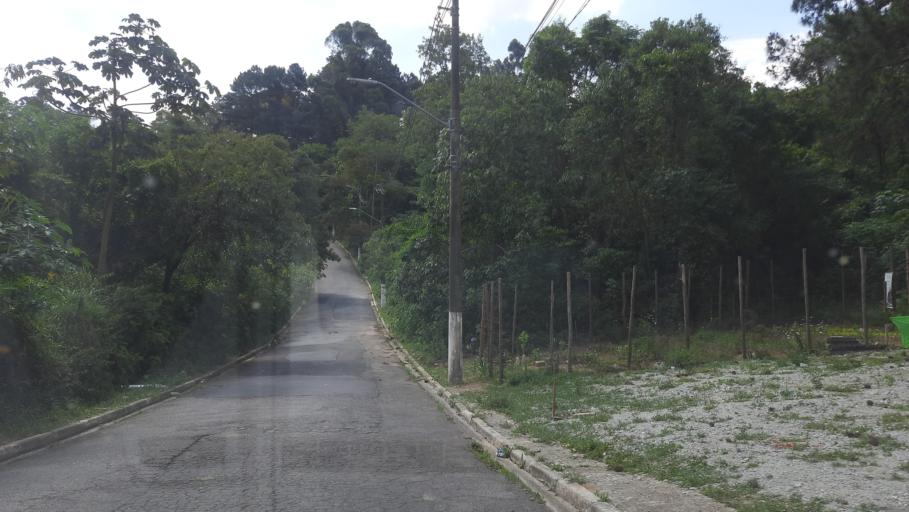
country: BR
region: Sao Paulo
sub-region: Caieiras
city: Caieiras
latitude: -23.4192
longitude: -46.7220
